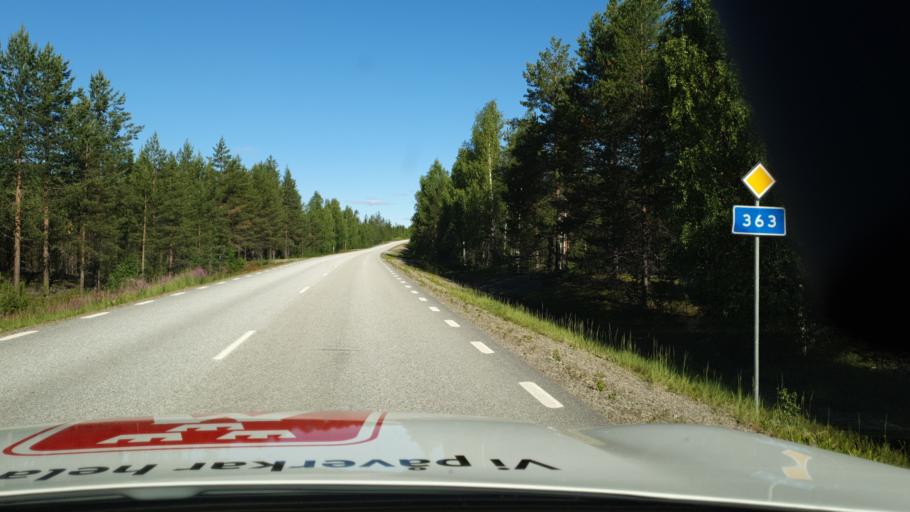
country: SE
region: Vaesterbotten
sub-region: Vindelns Kommun
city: Vindeln
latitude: 64.3284
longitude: 19.5208
